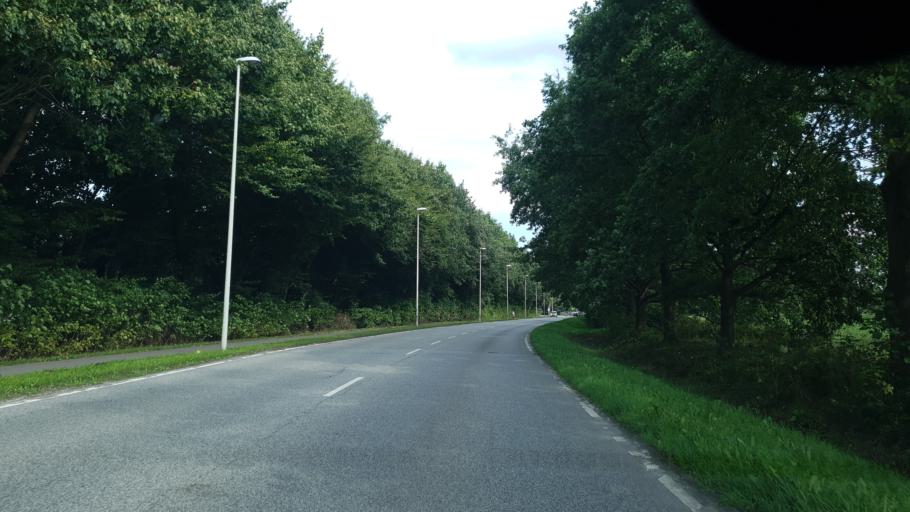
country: DE
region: Schleswig-Holstein
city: Kronshagen
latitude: 54.3503
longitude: 10.0819
